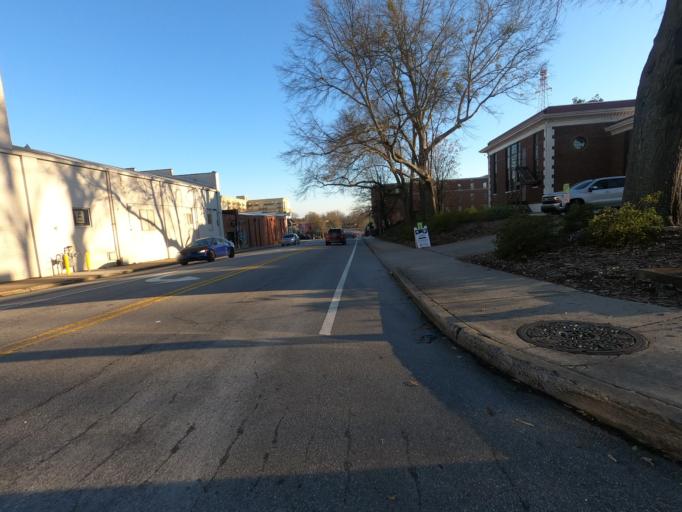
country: US
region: Georgia
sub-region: Clarke County
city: Athens
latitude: 33.9591
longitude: -83.3807
